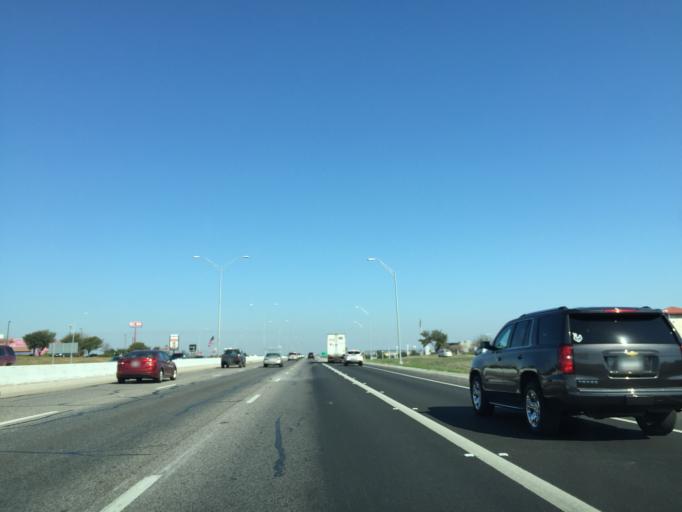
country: US
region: Texas
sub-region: Williamson County
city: Round Rock
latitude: 30.5377
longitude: -97.6921
